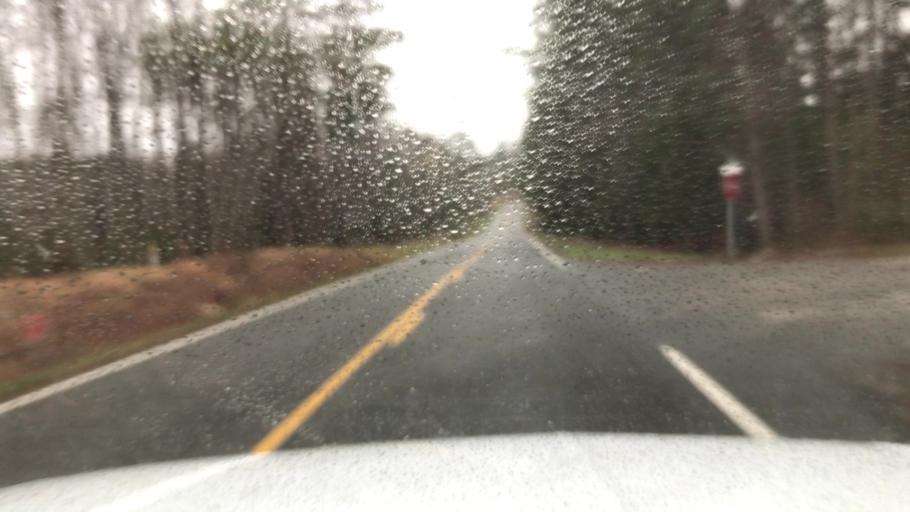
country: US
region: Virginia
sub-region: Henrico County
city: Short Pump
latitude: 37.6549
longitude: -77.6781
